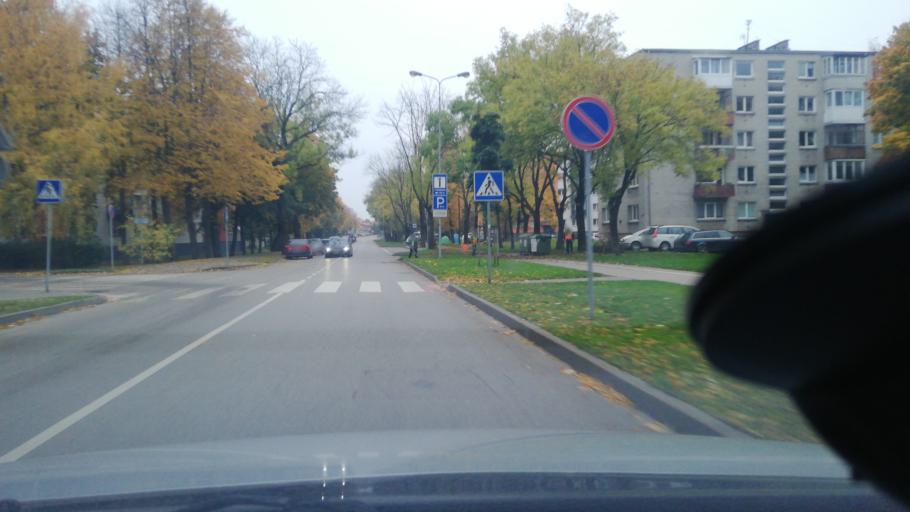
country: LT
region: Klaipedos apskritis
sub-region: Klaipeda
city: Klaipeda
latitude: 55.7266
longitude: 21.1316
